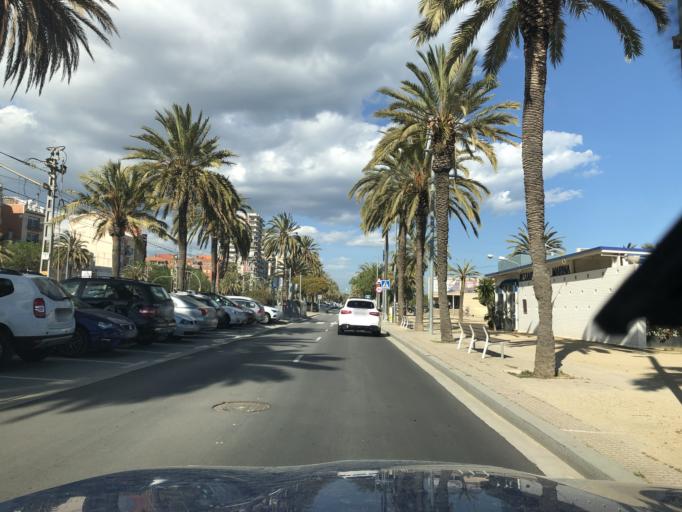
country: ES
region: Catalonia
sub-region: Provincia de Barcelona
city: Mataro
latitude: 41.5369
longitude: 2.4509
